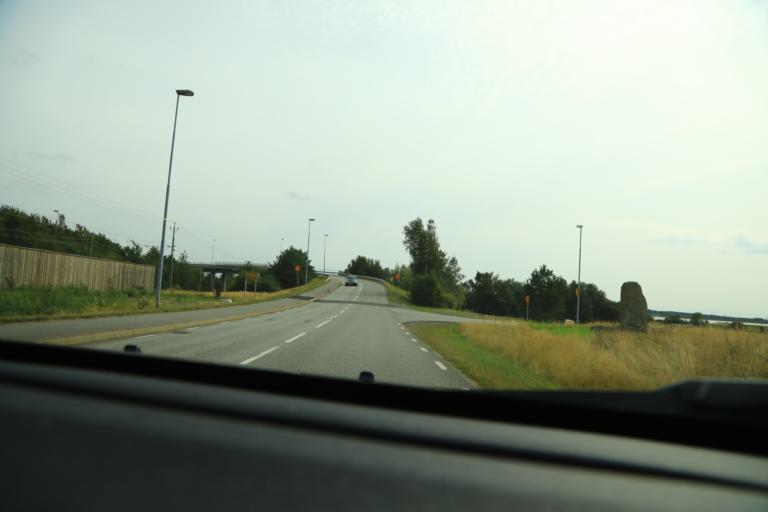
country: SE
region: Halland
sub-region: Varbergs Kommun
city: Varberg
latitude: 57.1716
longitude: 12.2283
